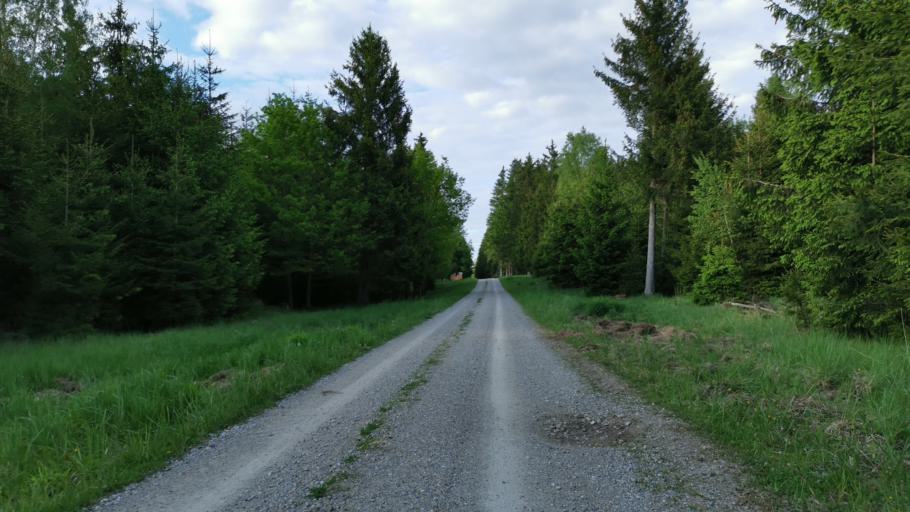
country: DE
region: Bavaria
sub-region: Upper Bavaria
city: Neuried
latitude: 48.0644
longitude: 11.4807
